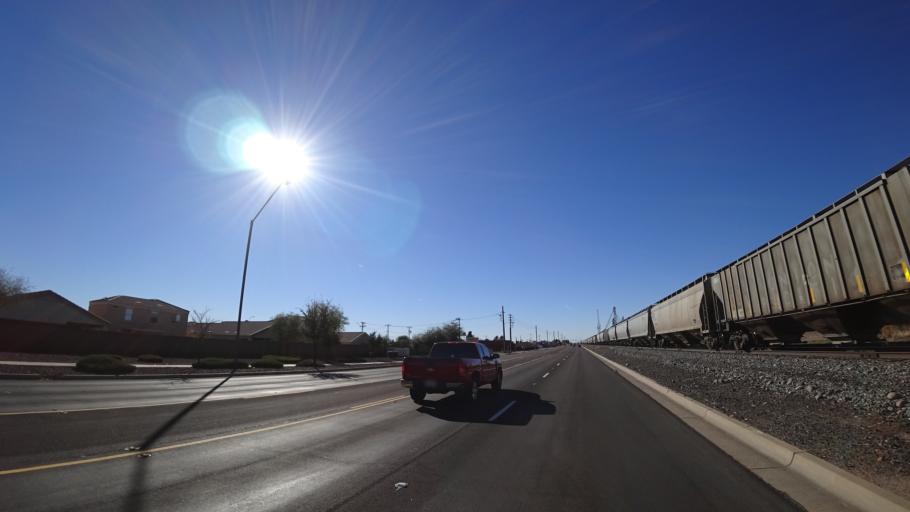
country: US
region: Arizona
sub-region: Maricopa County
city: Tolleson
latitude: 33.4355
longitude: -112.2928
